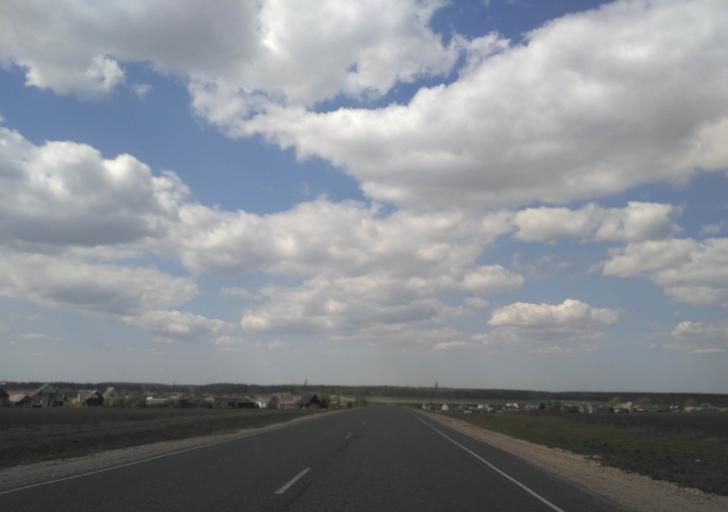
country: BY
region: Minsk
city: Vilyeyka
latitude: 54.5158
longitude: 26.9844
